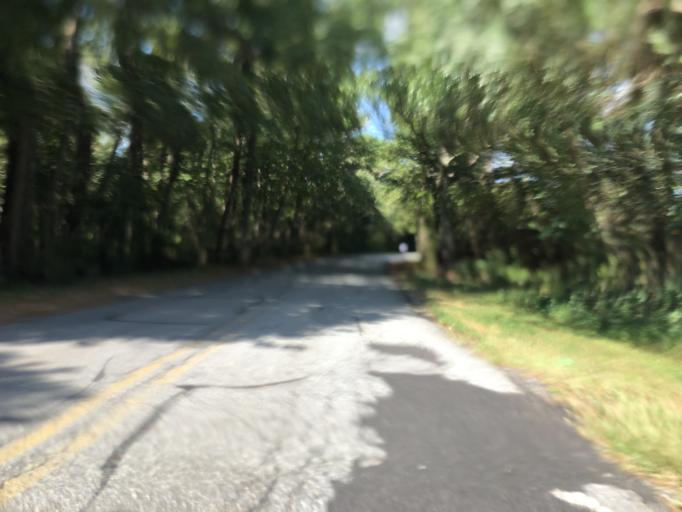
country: US
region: Georgia
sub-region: Fulton County
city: Palmetto
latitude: 33.5116
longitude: -84.6930
